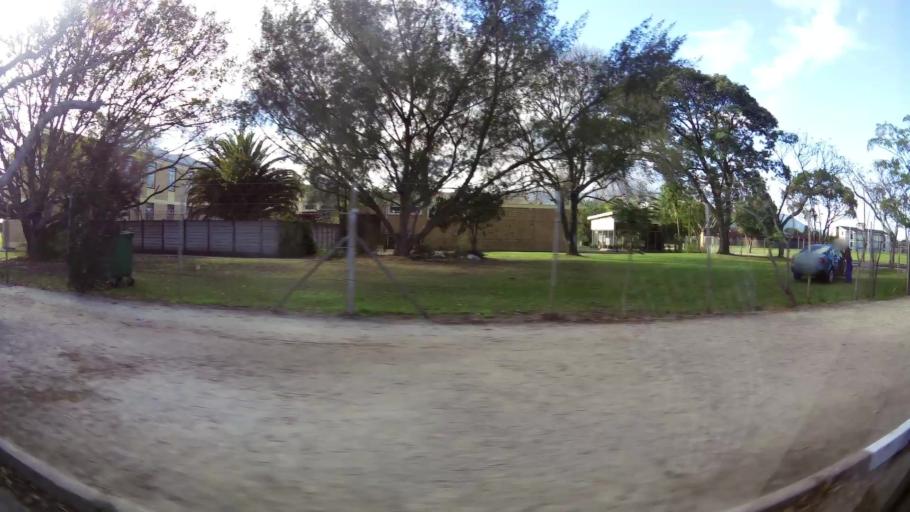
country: ZA
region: Western Cape
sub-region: Eden District Municipality
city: George
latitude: -33.9587
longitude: 22.4782
